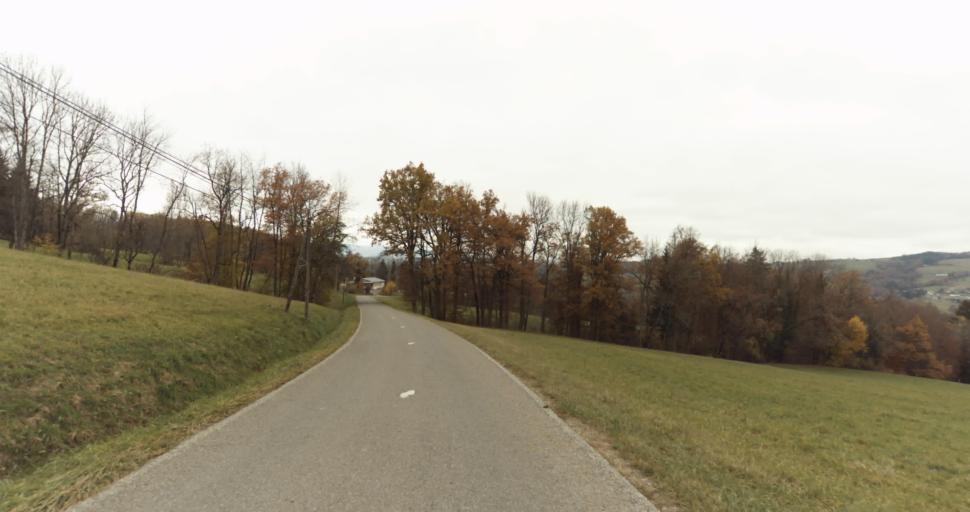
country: FR
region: Rhone-Alpes
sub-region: Departement de la Haute-Savoie
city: Thorens-Glieres
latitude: 45.9845
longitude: 6.2211
